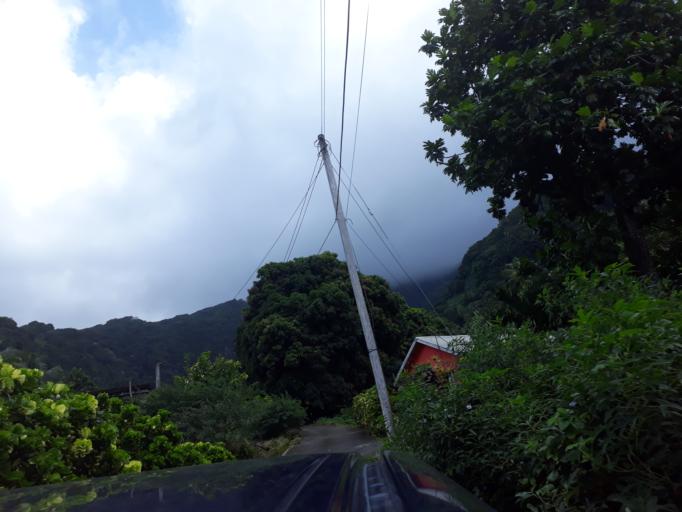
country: VC
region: Charlotte
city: Georgetown
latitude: 13.3787
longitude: -61.1705
